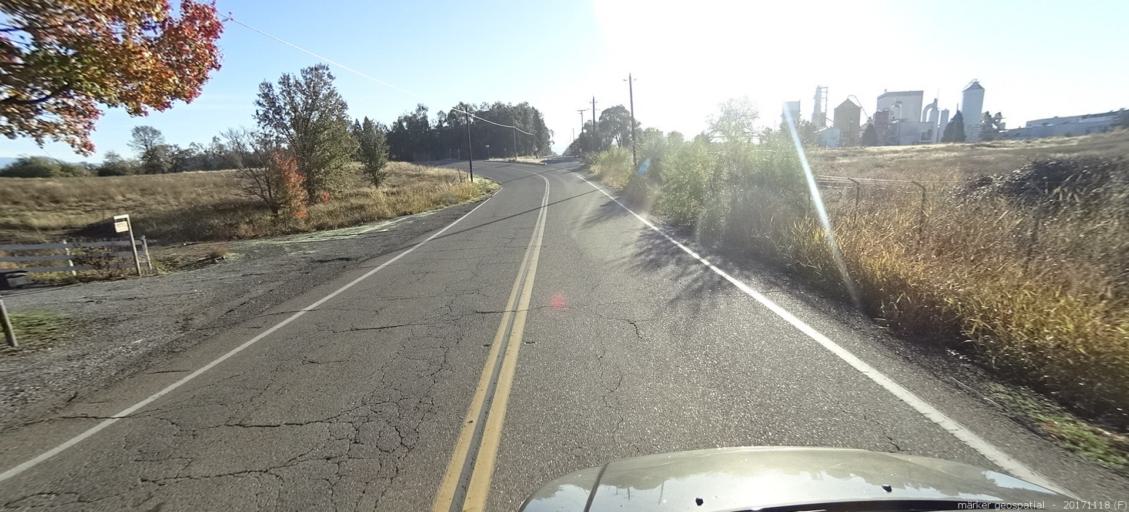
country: US
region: California
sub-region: Shasta County
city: Anderson
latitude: 40.4390
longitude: -122.2718
